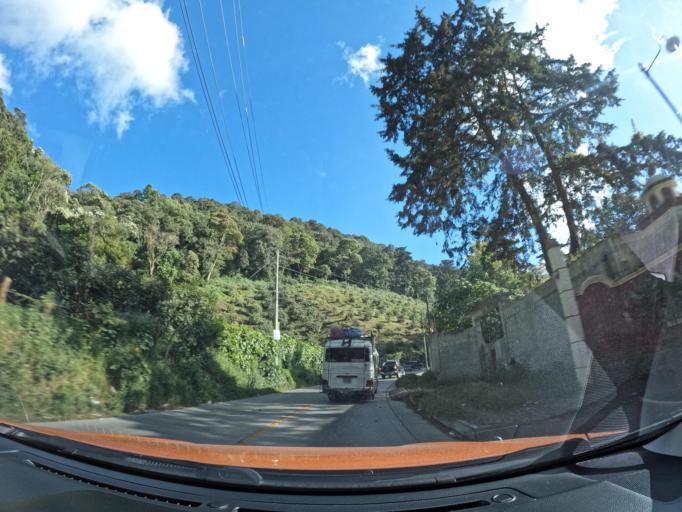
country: GT
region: Sacatepequez
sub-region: Municipio de Santa Maria de Jesus
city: Santa Maria de Jesus
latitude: 14.5020
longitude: -90.7100
